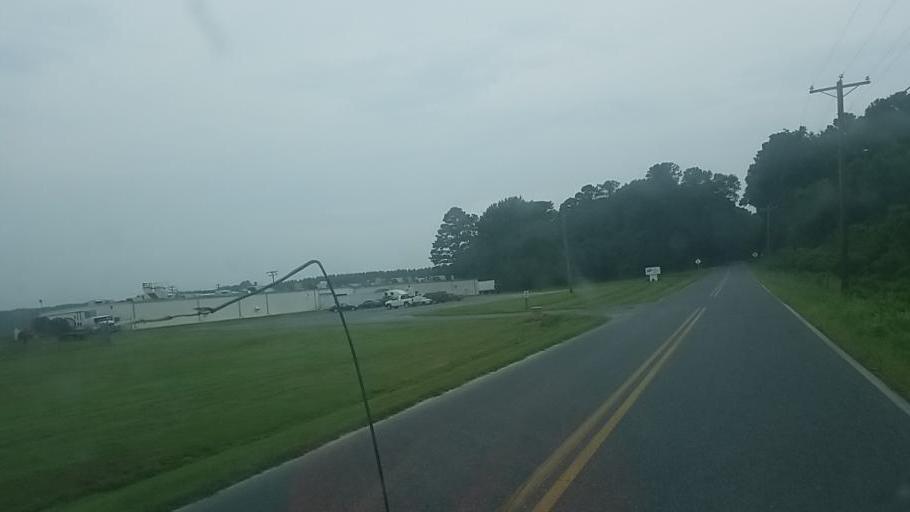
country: US
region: Maryland
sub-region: Wicomico County
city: Salisbury
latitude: 38.3853
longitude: -75.5274
